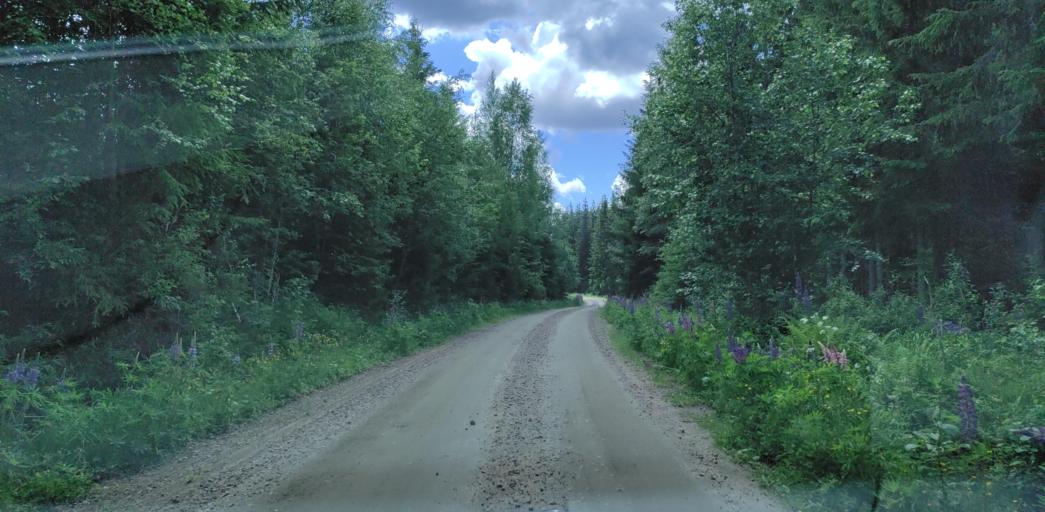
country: SE
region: Vaermland
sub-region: Hagfors Kommun
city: Ekshaerad
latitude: 60.0785
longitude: 13.3139
